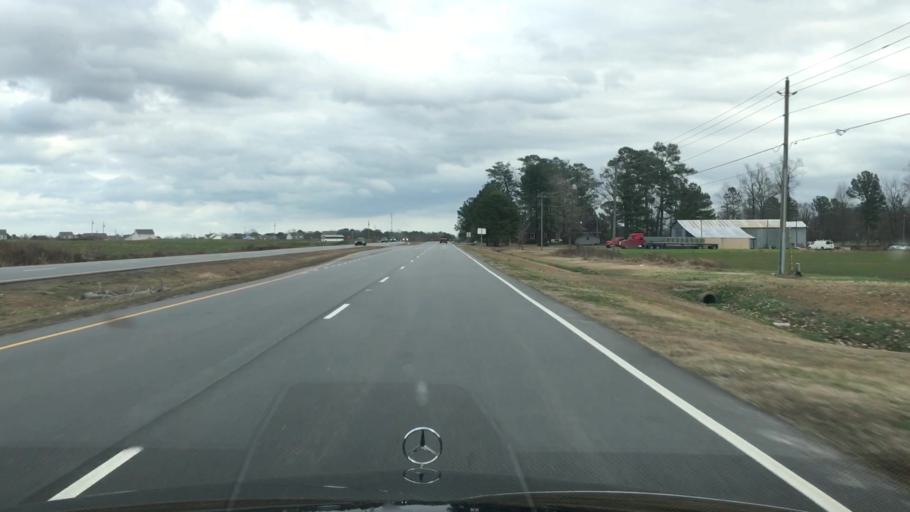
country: US
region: North Carolina
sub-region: Onslow County
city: Richlands
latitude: 34.9178
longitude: -77.6121
